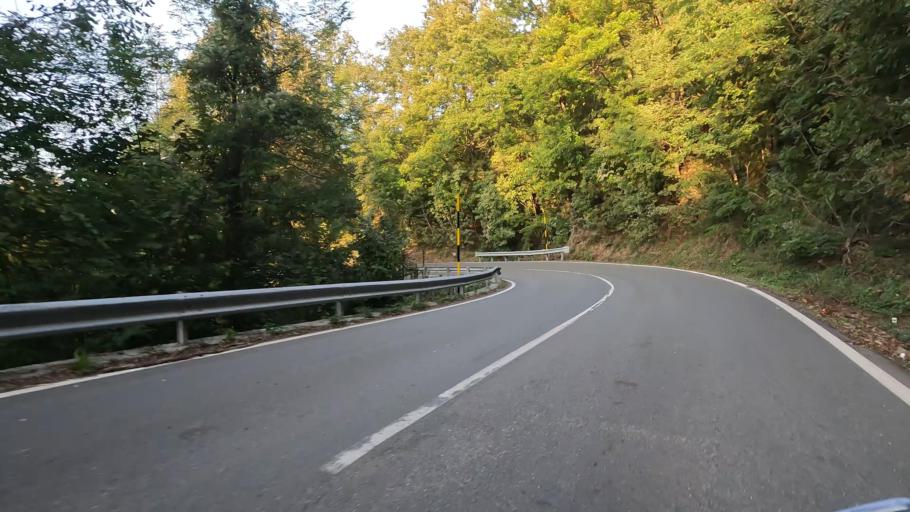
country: IT
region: Liguria
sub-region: Provincia di Savona
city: Sassello
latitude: 44.4879
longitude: 8.4972
